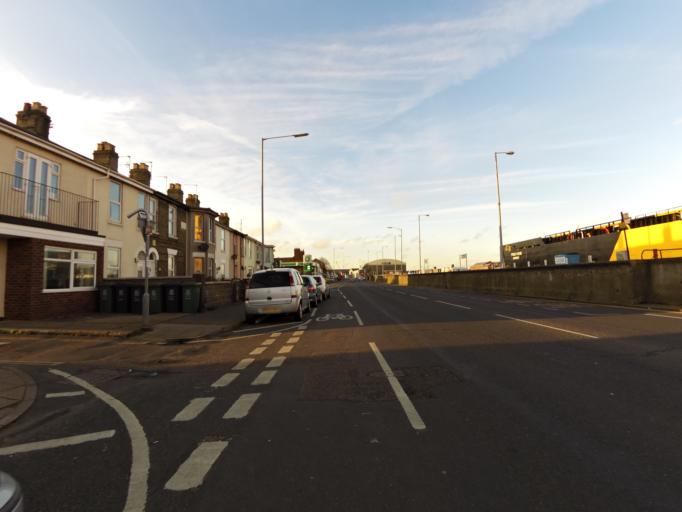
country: GB
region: England
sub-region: Norfolk
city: Great Yarmouth
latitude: 52.5936
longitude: 1.7250
